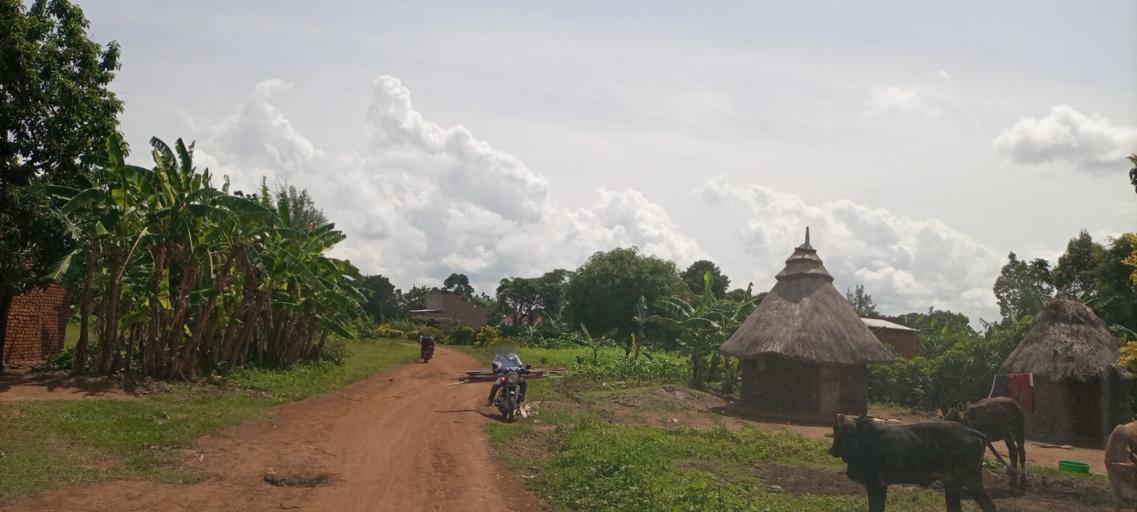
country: UG
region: Eastern Region
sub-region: Budaka District
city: Budaka
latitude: 1.1713
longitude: 33.9354
